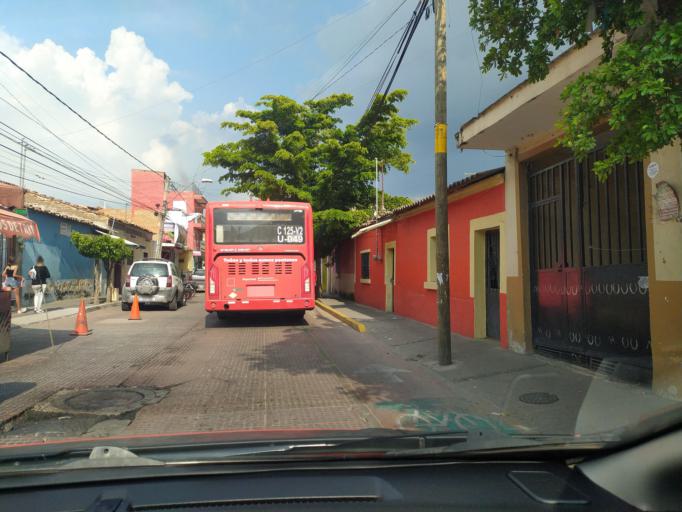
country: MX
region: Jalisco
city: Tlajomulco de Zuniga
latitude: 20.4766
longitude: -103.4504
